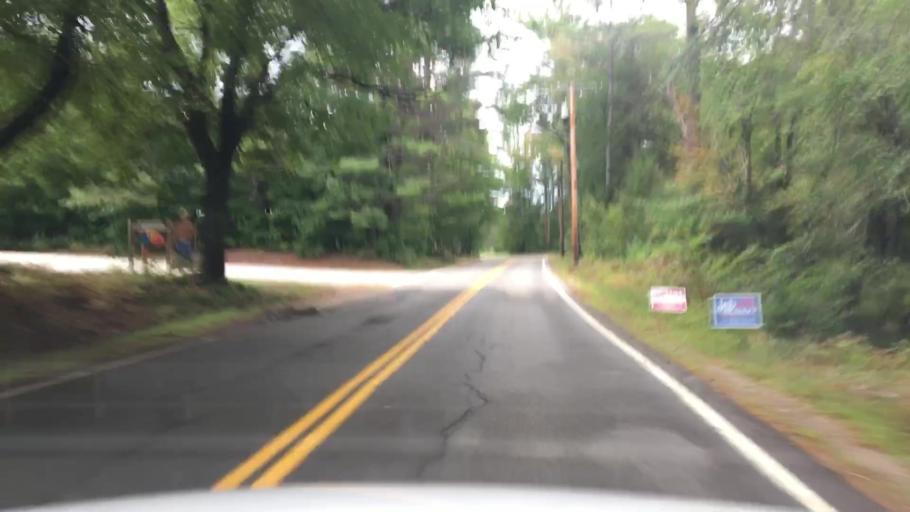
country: US
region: New Hampshire
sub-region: Carroll County
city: Effingham
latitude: 43.7346
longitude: -71.0066
